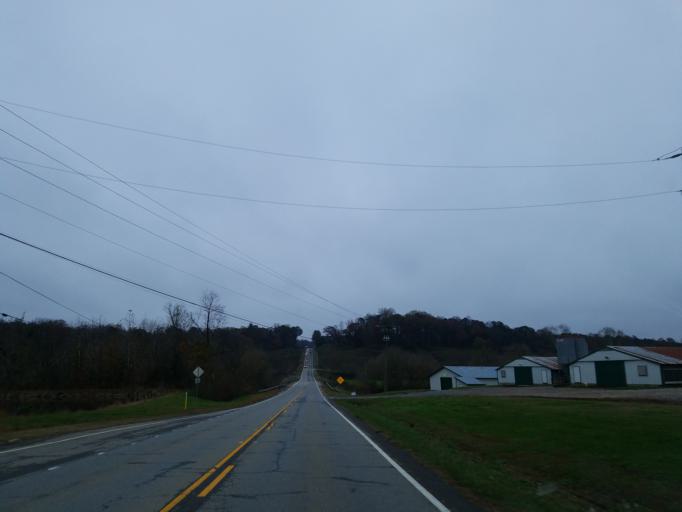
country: US
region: Georgia
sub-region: Pickens County
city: Nelson
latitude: 34.4012
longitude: -84.4306
